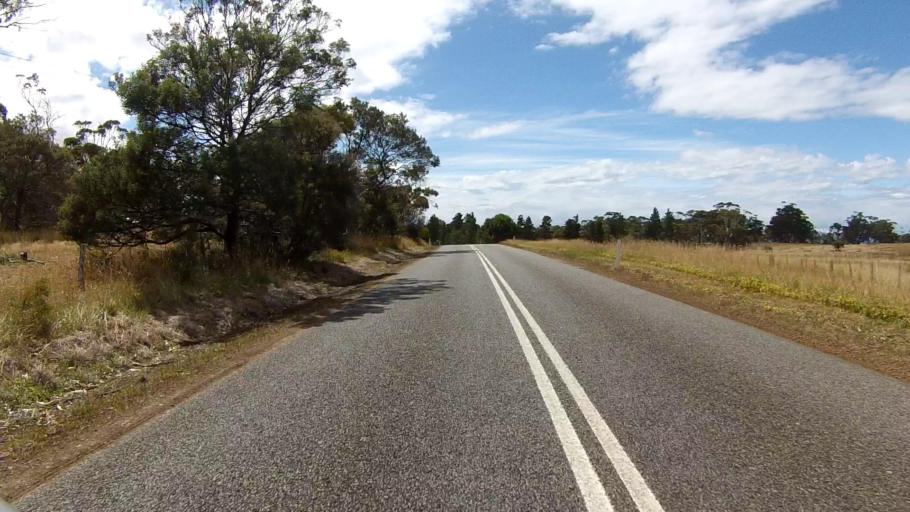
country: AU
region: Tasmania
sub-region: Sorell
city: Sorell
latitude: -42.2885
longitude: 147.9950
